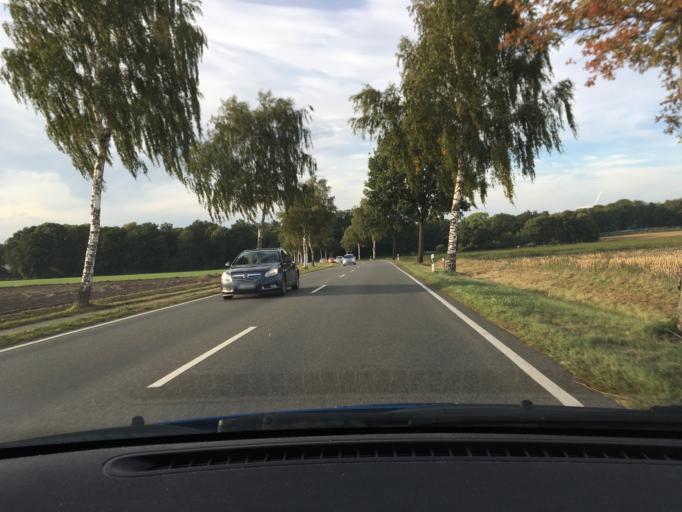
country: DE
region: Lower Saxony
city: Soltau
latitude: 52.9952
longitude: 9.9045
